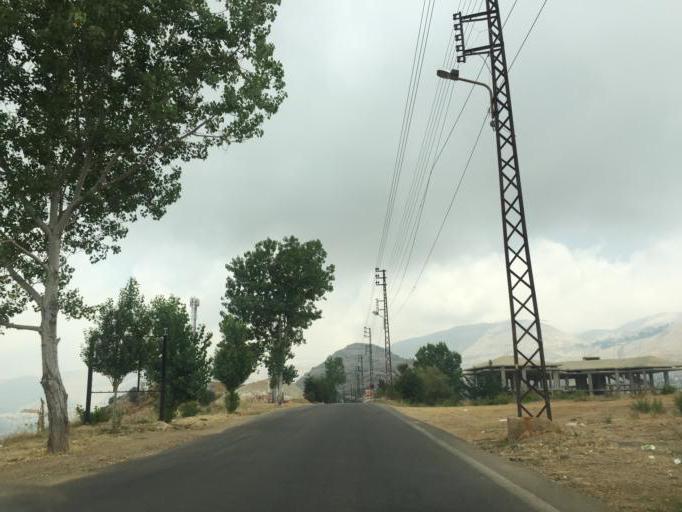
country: LB
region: Mont-Liban
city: Djounie
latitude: 33.9997
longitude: 35.7997
